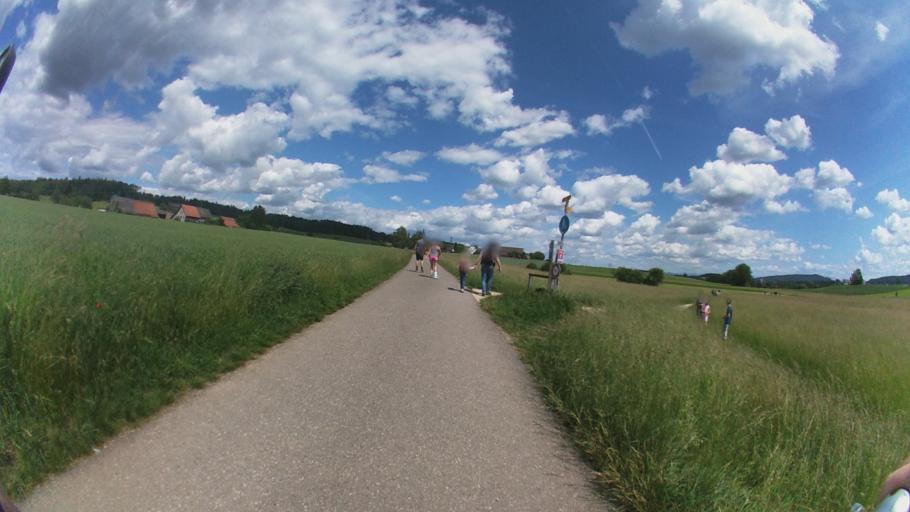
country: CH
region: Zurich
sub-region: Bezirk Zuerich
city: Zuerich (Kreis 11) / Affoltern
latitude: 47.4364
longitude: 8.5000
